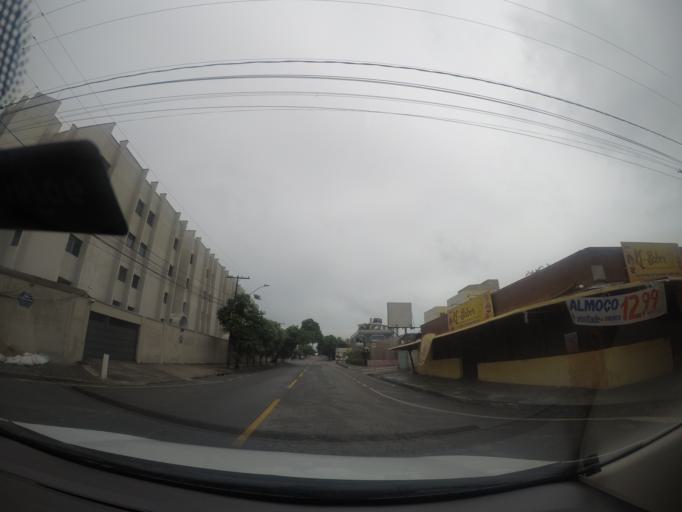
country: BR
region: Goias
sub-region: Goiania
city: Goiania
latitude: -16.7119
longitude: -49.2837
